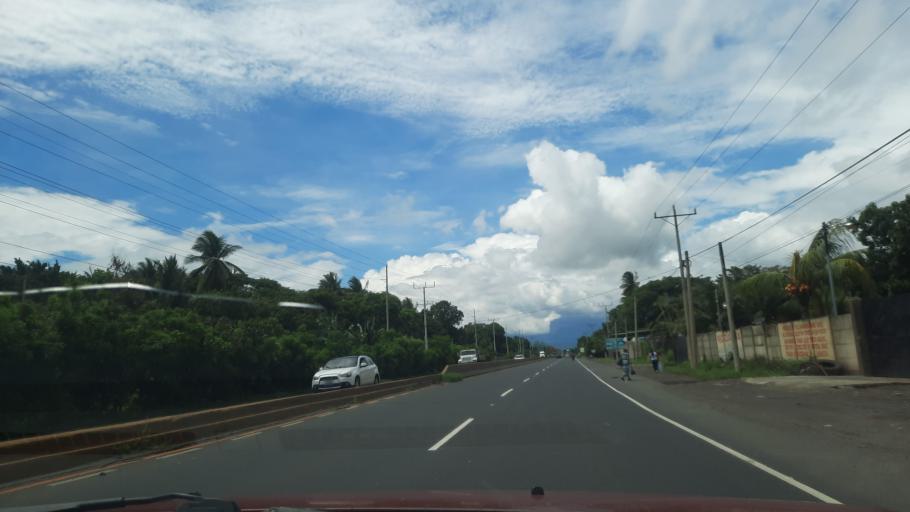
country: SV
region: Sonsonate
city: San Antonio del Monte
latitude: 13.6472
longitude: -89.7702
